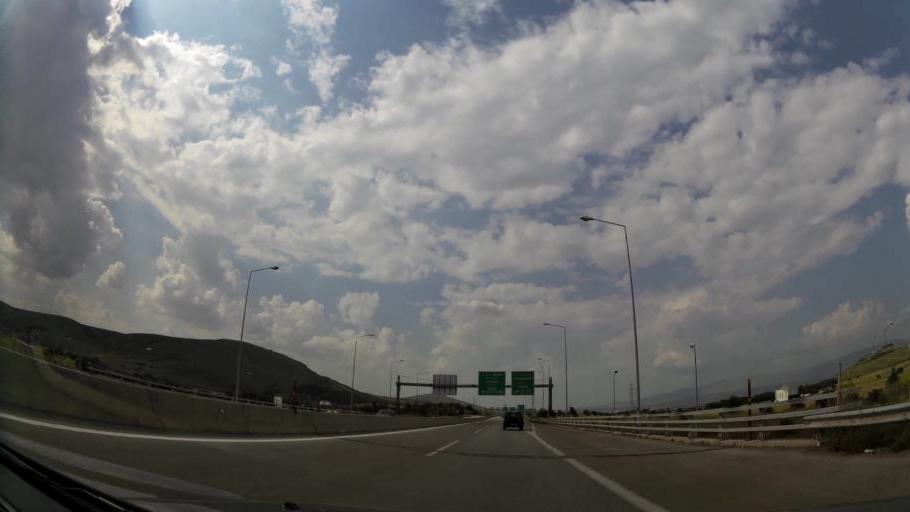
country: GR
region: West Macedonia
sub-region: Nomos Kozanis
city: Koila
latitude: 40.3437
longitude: 21.8065
